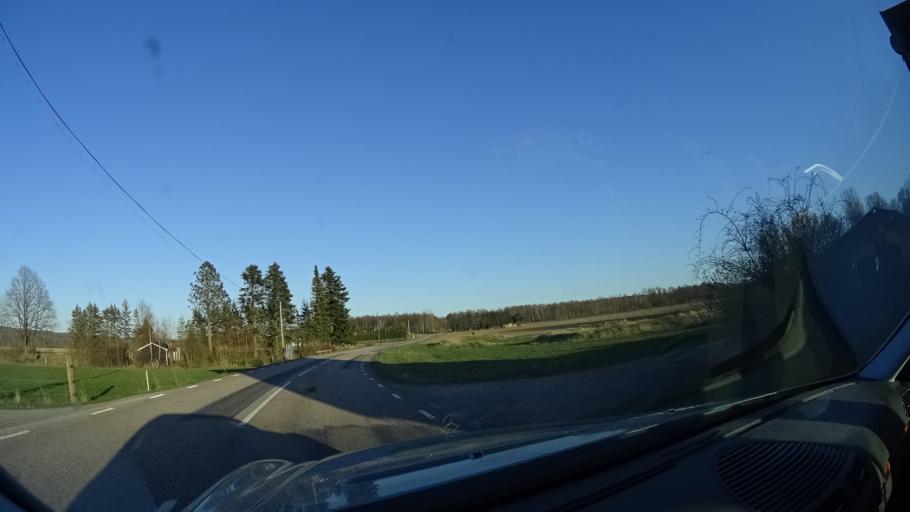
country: SE
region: Skane
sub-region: Bjuvs Kommun
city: Billesholm
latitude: 56.0370
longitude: 13.0247
